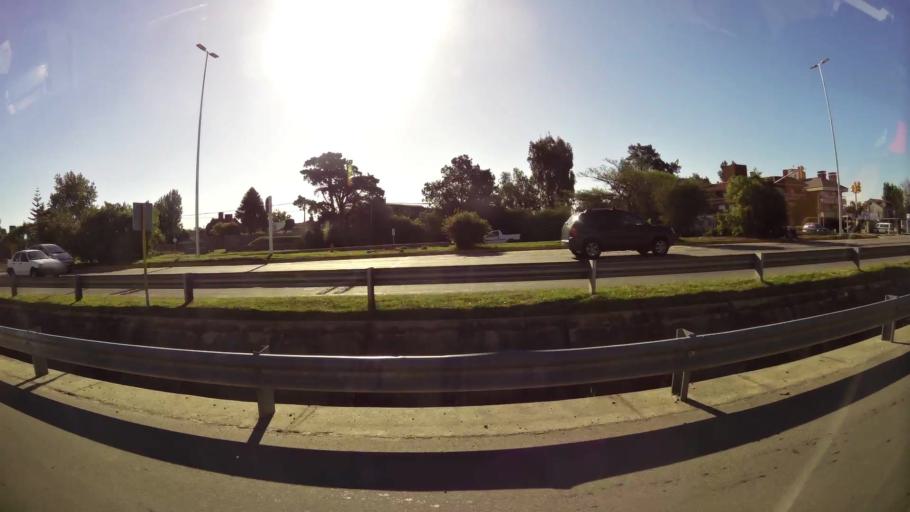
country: UY
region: Canelones
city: Barra de Carrasco
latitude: -34.8654
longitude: -56.0307
